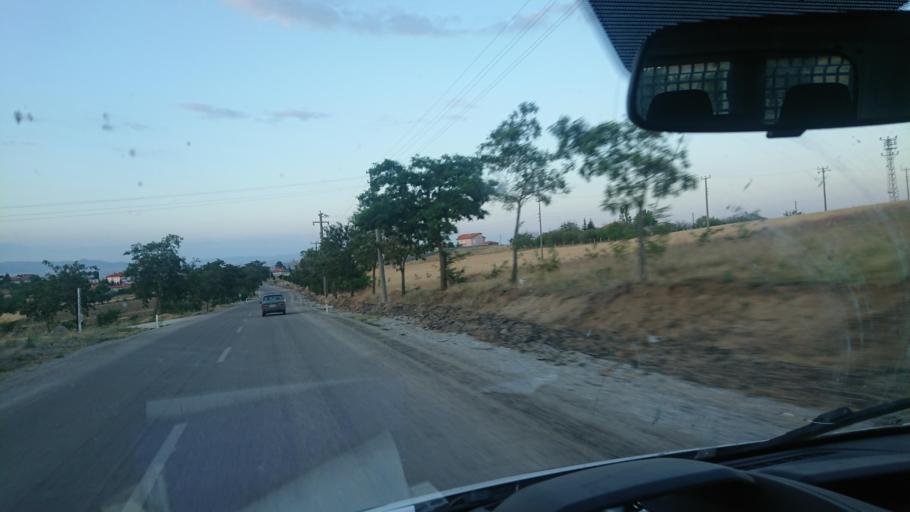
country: TR
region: Aksaray
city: Sariyahsi
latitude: 38.9748
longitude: 33.8337
